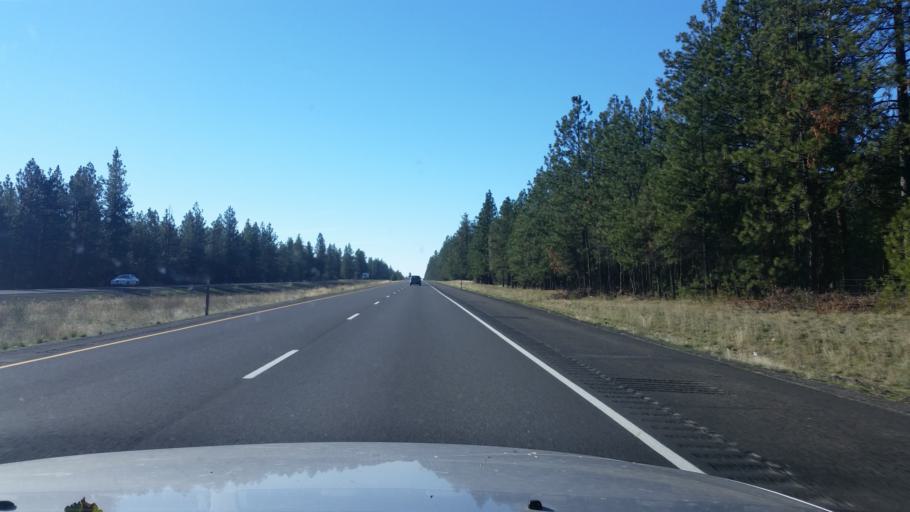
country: US
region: Washington
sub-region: Spokane County
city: Medical Lake
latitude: 47.4859
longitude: -117.7183
